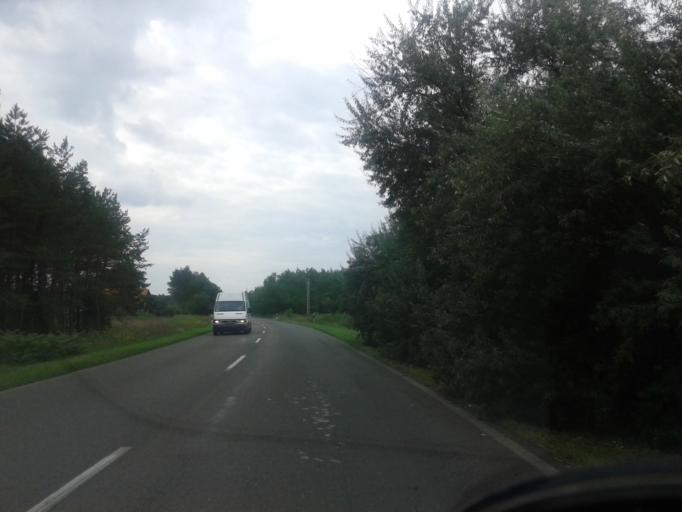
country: HU
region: Csongrad
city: Asotthalom
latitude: 46.2296
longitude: 19.7527
